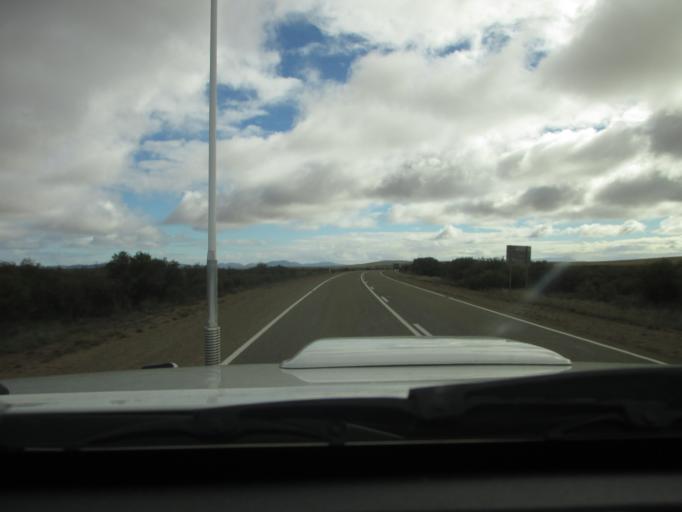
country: AU
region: South Australia
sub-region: Flinders Ranges
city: Quorn
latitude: -32.1218
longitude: 138.5070
